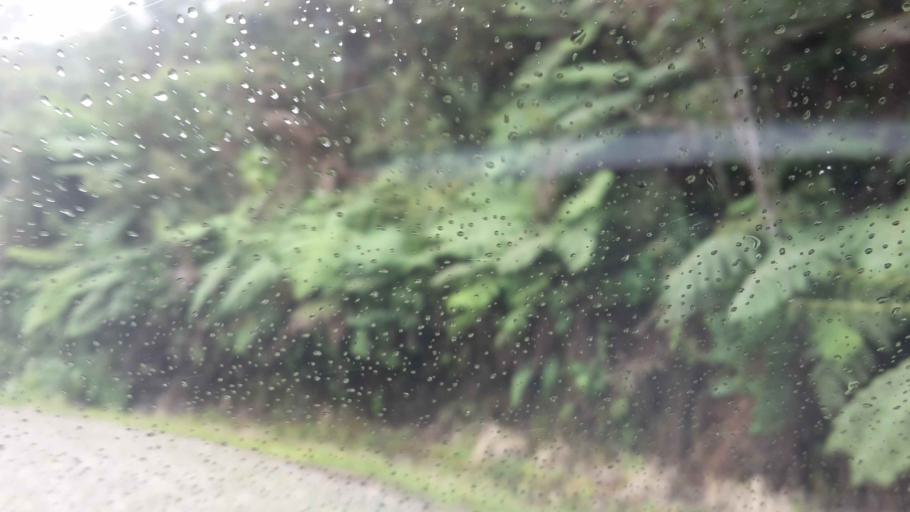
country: BO
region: Cochabamba
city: Colomi
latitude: -17.1667
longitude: -65.8951
